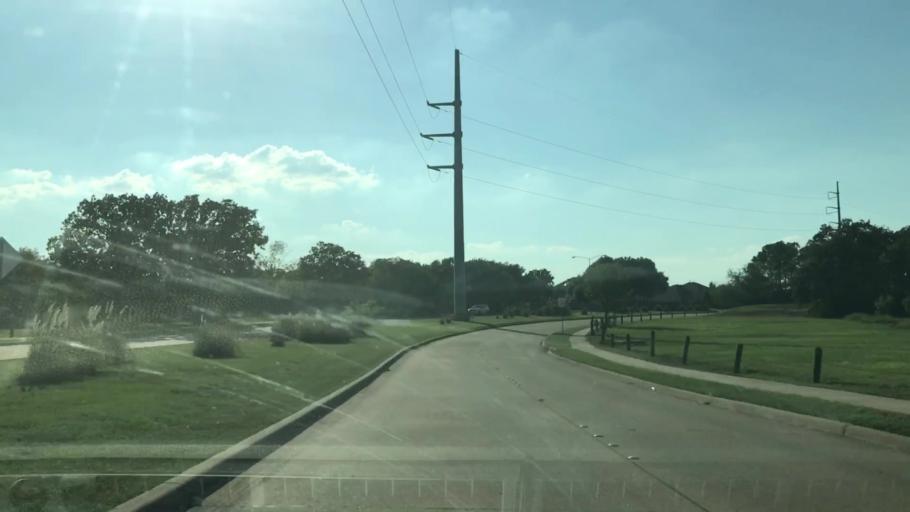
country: US
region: Texas
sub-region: Denton County
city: Lewisville
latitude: 33.0278
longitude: -97.0284
